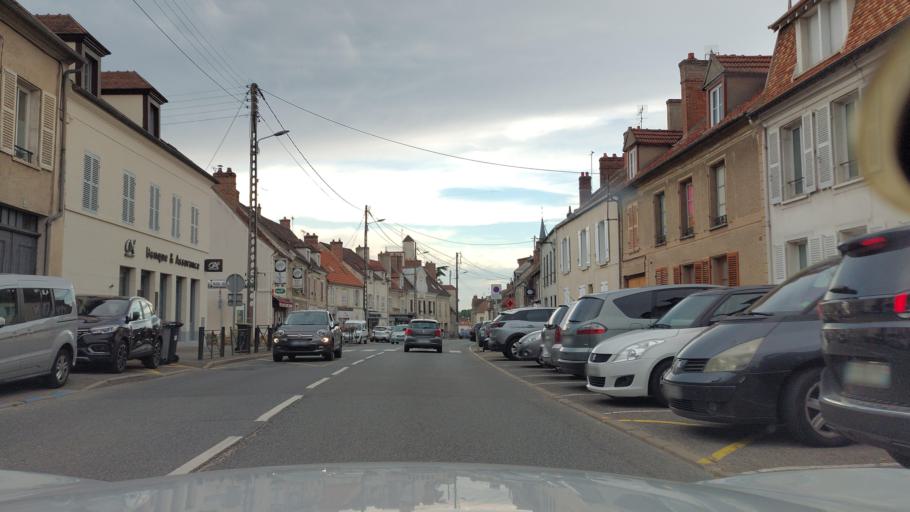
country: FR
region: Ile-de-France
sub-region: Departement de Seine-et-Marne
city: Guignes
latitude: 48.6353
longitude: 2.8001
